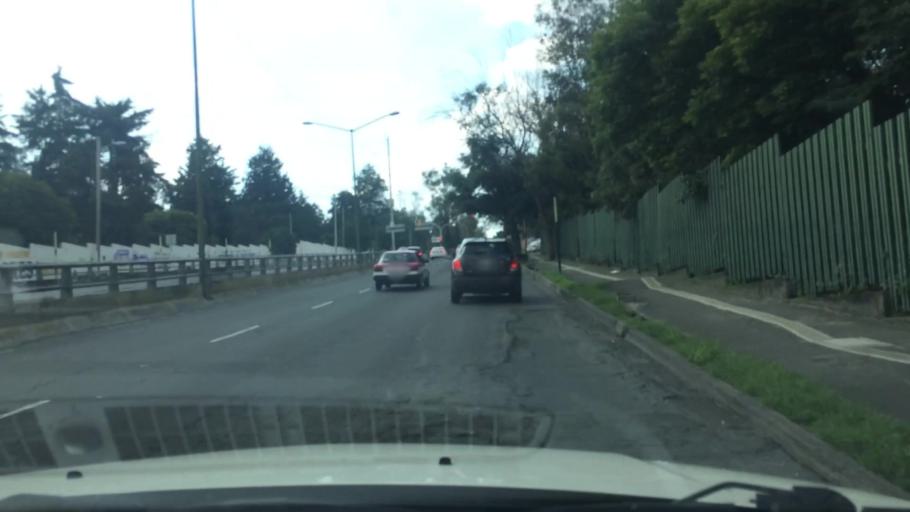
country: MX
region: Mexico City
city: Alvaro Obregon
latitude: 19.3515
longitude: -99.2061
